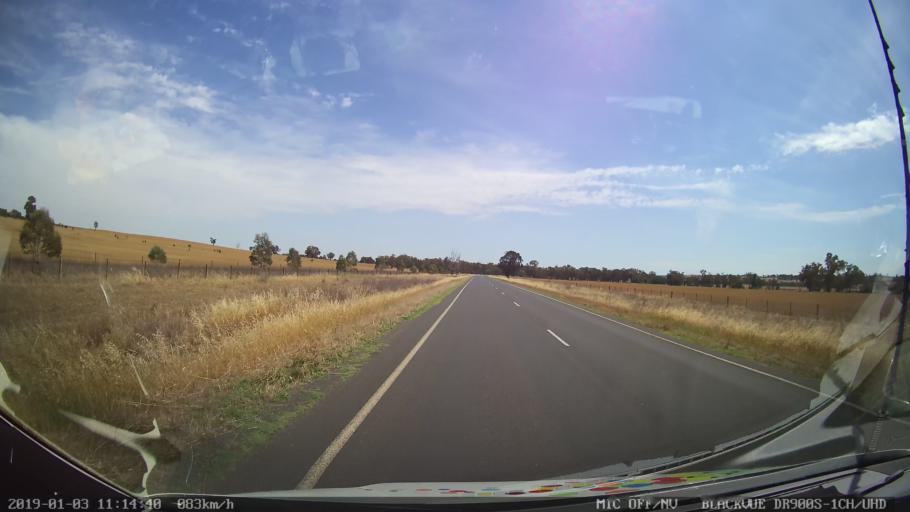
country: AU
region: New South Wales
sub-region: Young
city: Young
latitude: -34.1731
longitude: 148.2612
